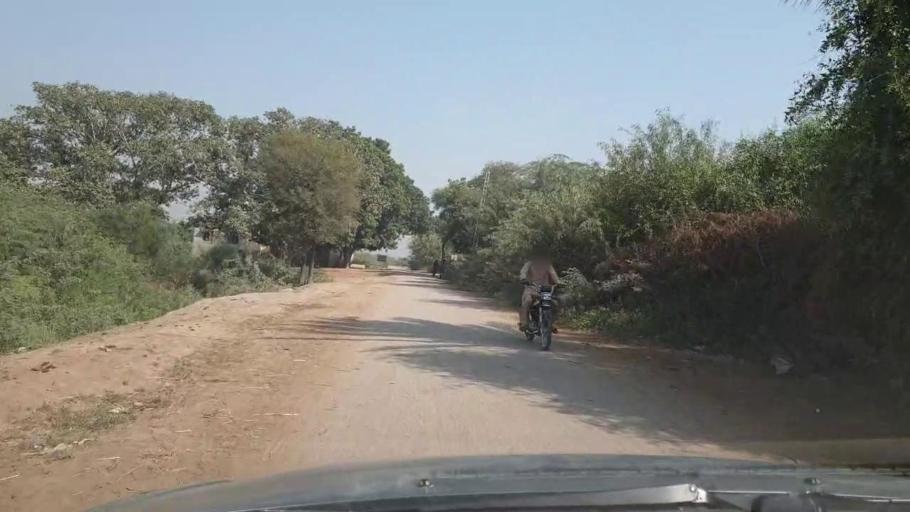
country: PK
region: Sindh
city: Tando Jam
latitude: 25.2955
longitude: 68.5307
